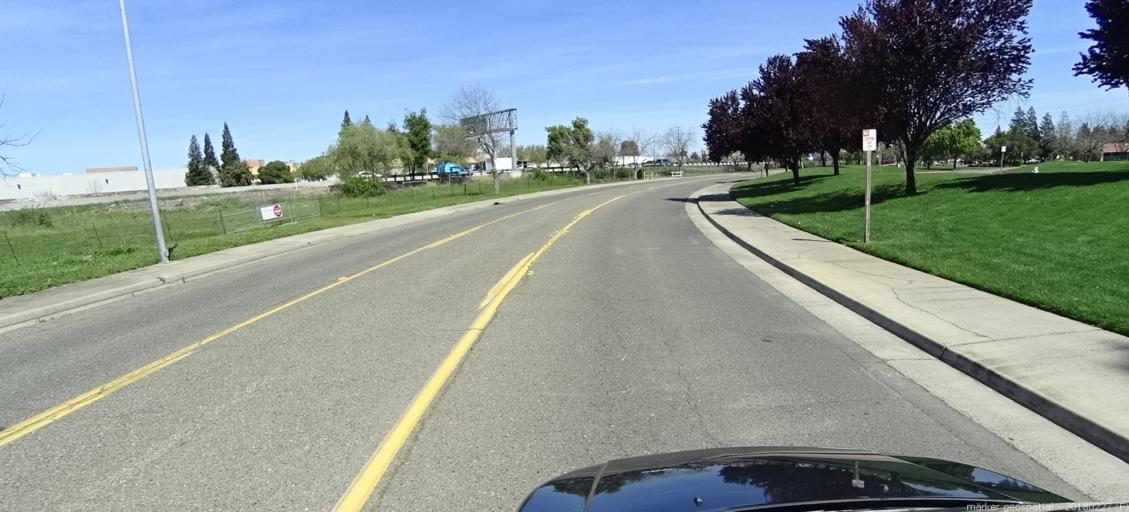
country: US
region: California
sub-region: Sacramento County
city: La Riviera
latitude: 38.5613
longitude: -121.3468
